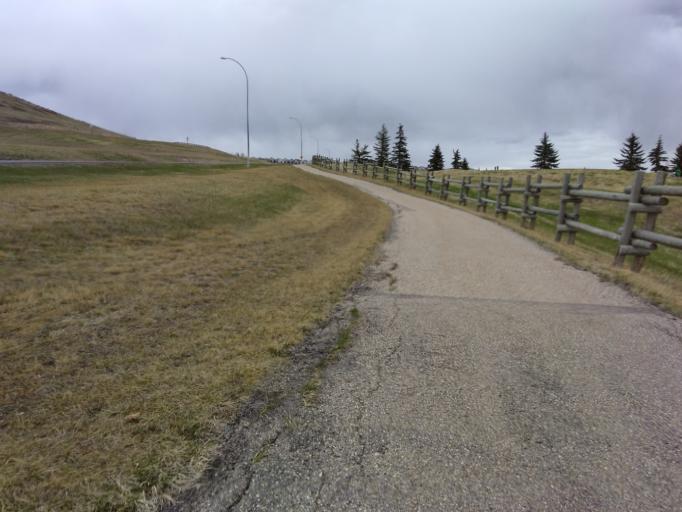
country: CA
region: Alberta
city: Cochrane
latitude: 51.1906
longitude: -114.4465
